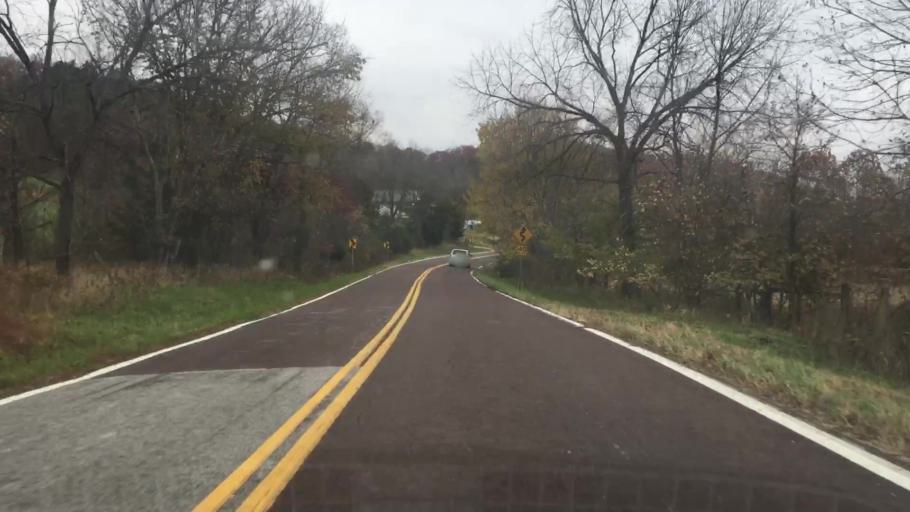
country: US
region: Missouri
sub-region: Callaway County
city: Fulton
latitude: 38.7960
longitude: -91.8721
